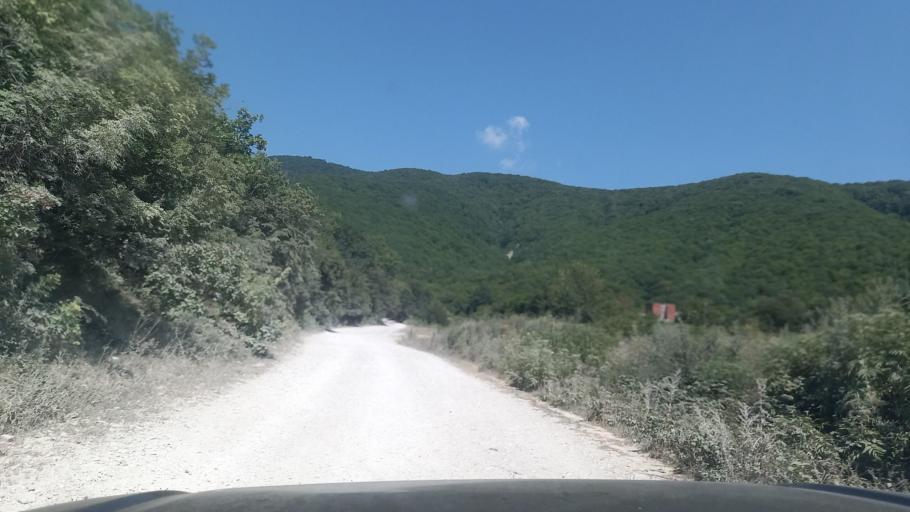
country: RU
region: Krasnodarskiy
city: Lermontovo
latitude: 44.3264
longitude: 38.7966
